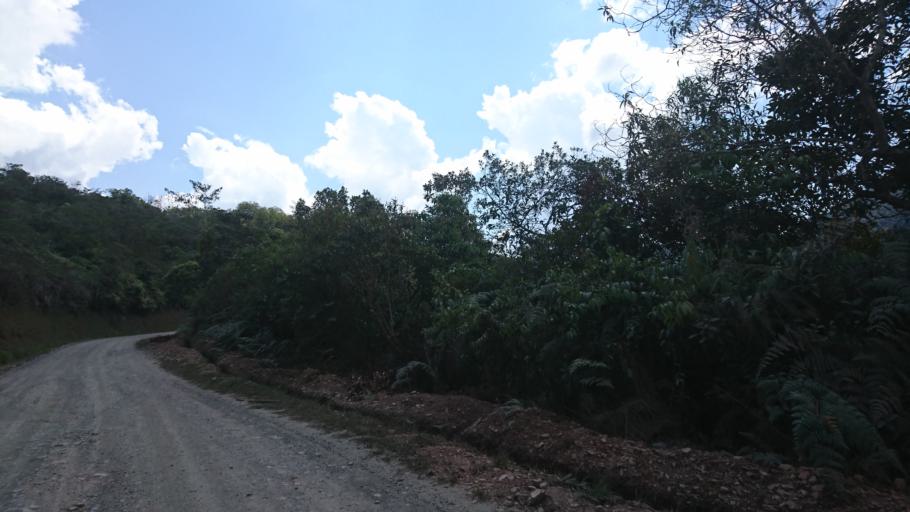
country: BO
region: La Paz
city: Coroico
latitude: -16.0751
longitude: -67.7814
